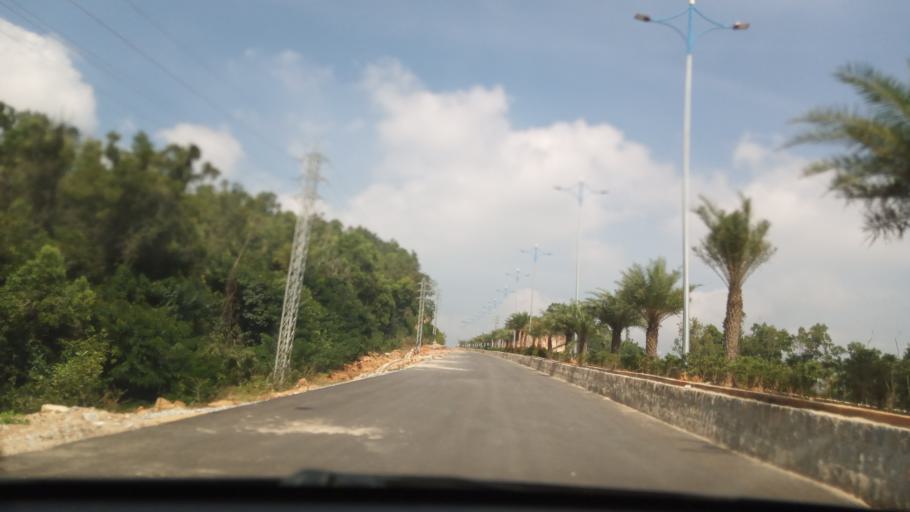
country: IN
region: Andhra Pradesh
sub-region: Chittoor
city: Tirumala
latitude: 13.6831
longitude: 79.3405
